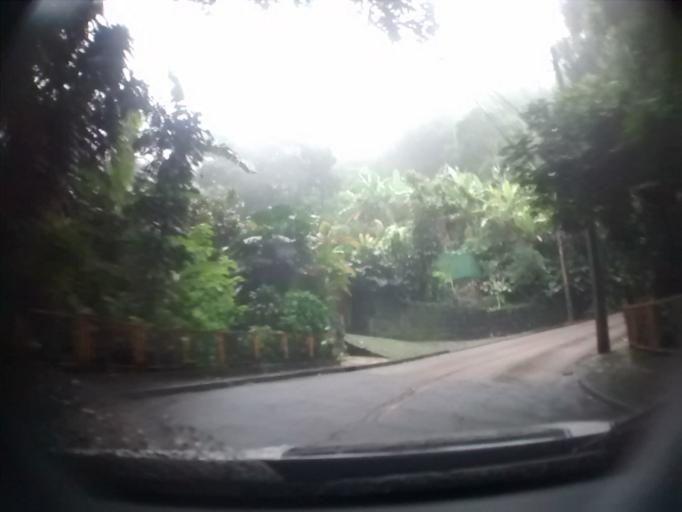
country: BR
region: Rio de Janeiro
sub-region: Rio De Janeiro
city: Rio de Janeiro
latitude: -22.9857
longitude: -43.2729
